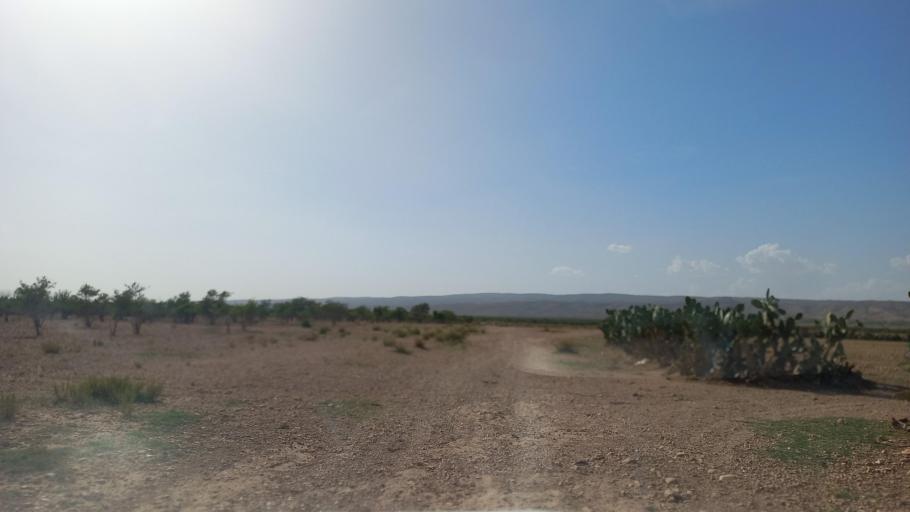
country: TN
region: Al Qasrayn
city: Kasserine
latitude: 35.3140
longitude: 9.0107
